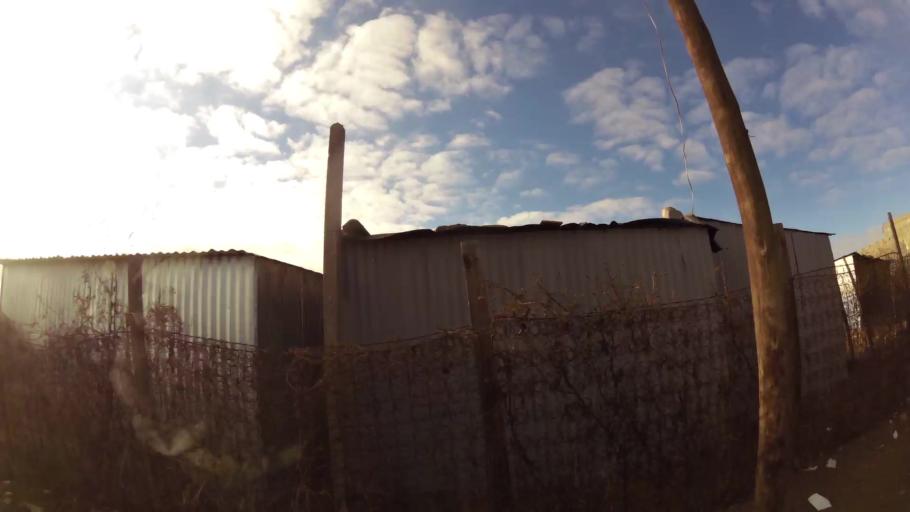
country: ZA
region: Gauteng
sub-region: Ekurhuleni Metropolitan Municipality
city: Tembisa
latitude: -26.0353
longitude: 28.1892
